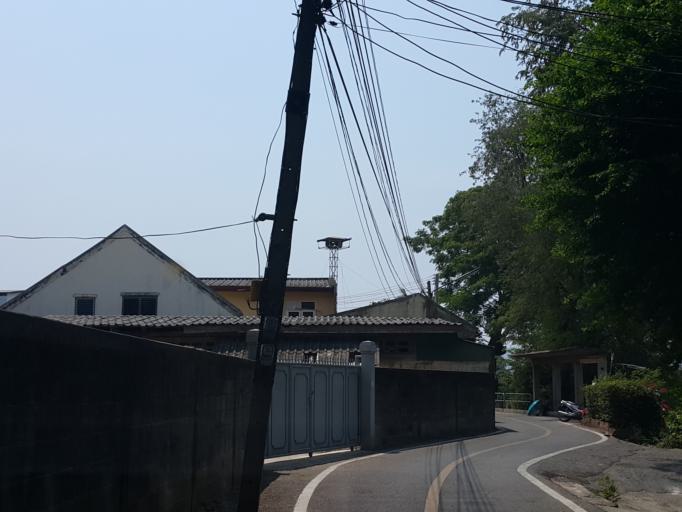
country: TH
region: Kanchanaburi
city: Kanchanaburi
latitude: 14.0294
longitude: 99.5234
